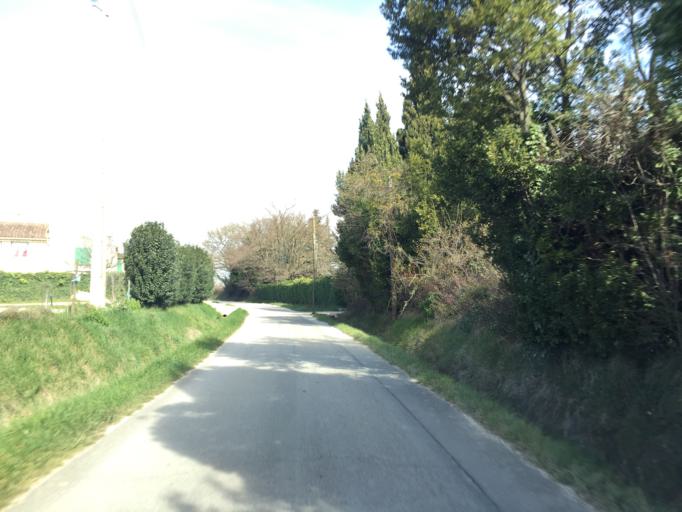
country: FR
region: Provence-Alpes-Cote d'Azur
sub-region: Departement du Vaucluse
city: Caderousse
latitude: 44.1205
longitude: 4.7429
